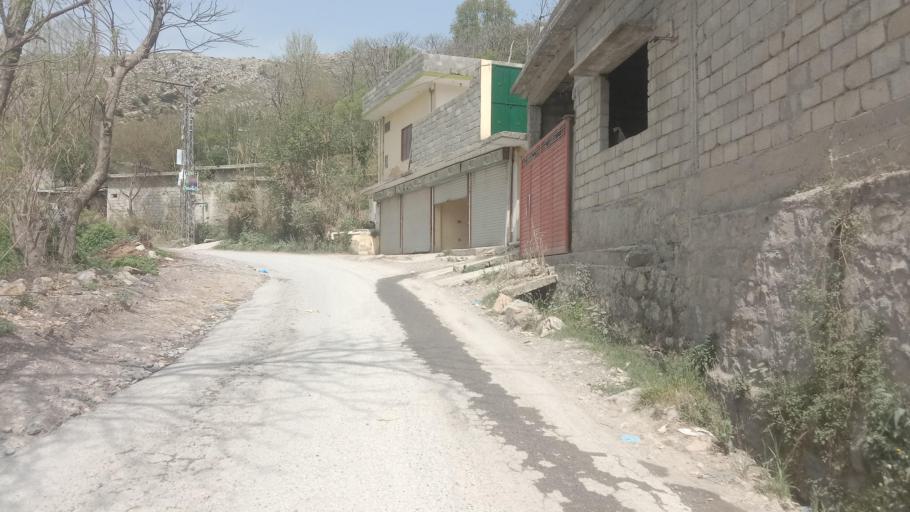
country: PK
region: Khyber Pakhtunkhwa
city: Abbottabad
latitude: 34.1663
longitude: 73.2822
